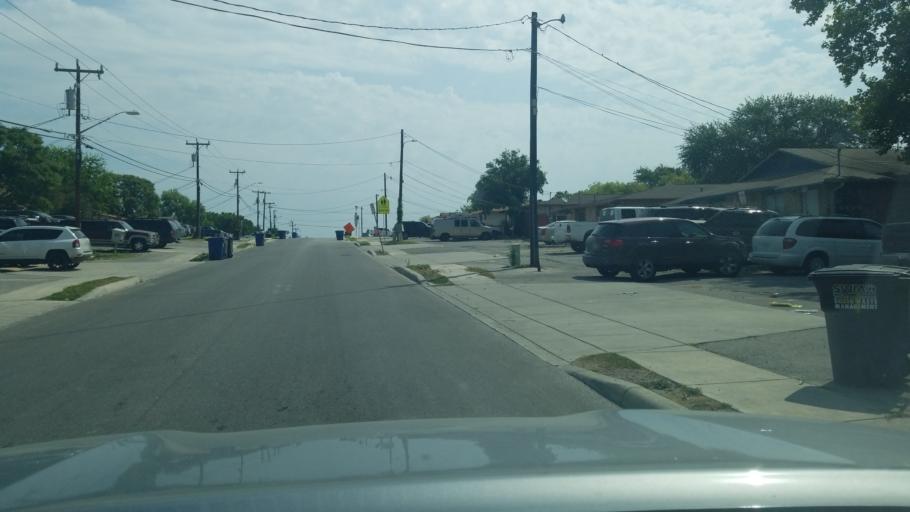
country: US
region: Texas
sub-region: Bexar County
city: Castle Hills
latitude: 29.5416
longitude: -98.5251
